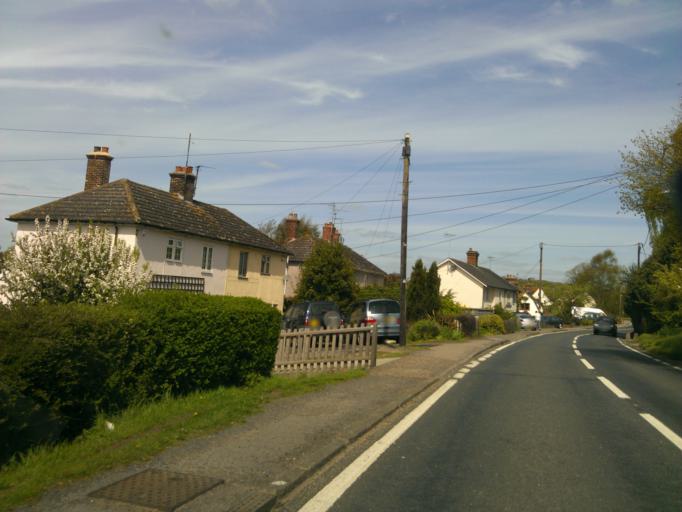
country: GB
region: England
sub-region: Essex
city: Marks Tey
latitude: 51.9191
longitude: 0.7634
